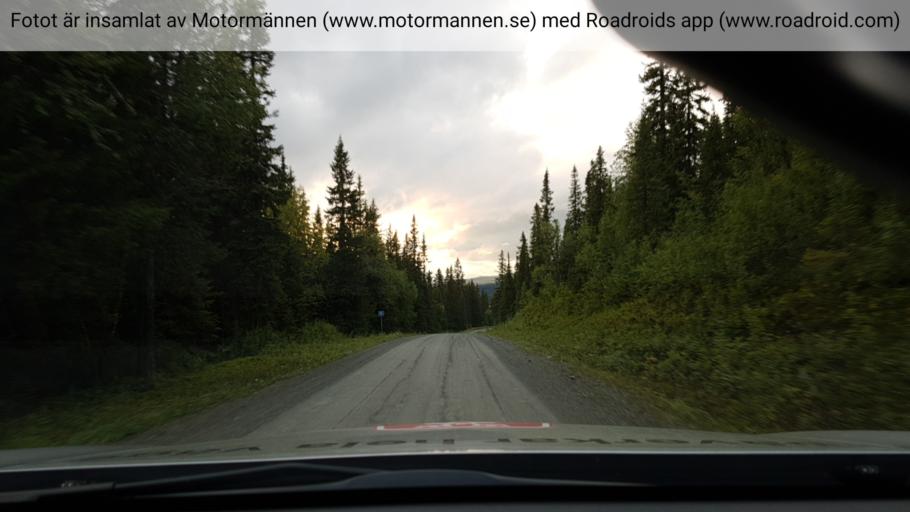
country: SE
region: Vaesterbotten
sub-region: Vilhelmina Kommun
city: Sjoberg
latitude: 65.4949
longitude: 15.4913
